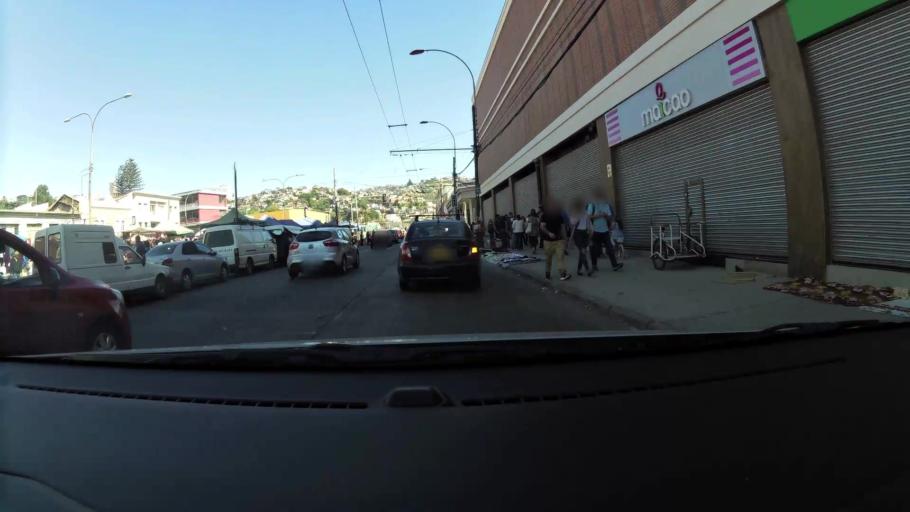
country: CL
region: Valparaiso
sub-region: Provincia de Valparaiso
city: Valparaiso
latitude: -33.0487
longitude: -71.6037
